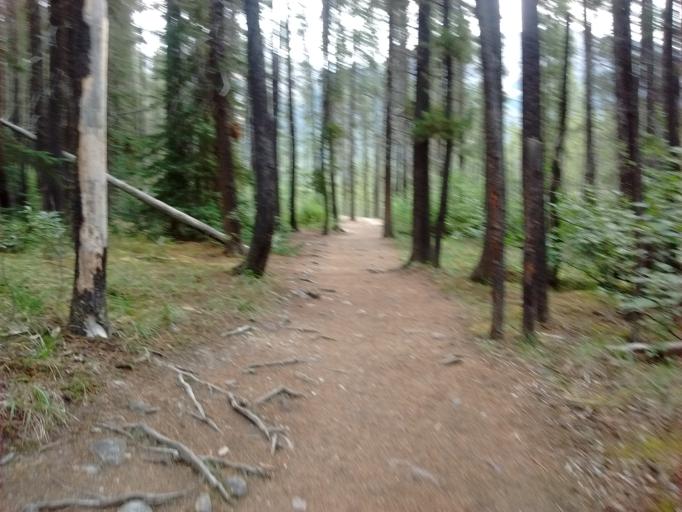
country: CA
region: Alberta
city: Jasper Park Lodge
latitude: 52.5314
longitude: -117.6460
